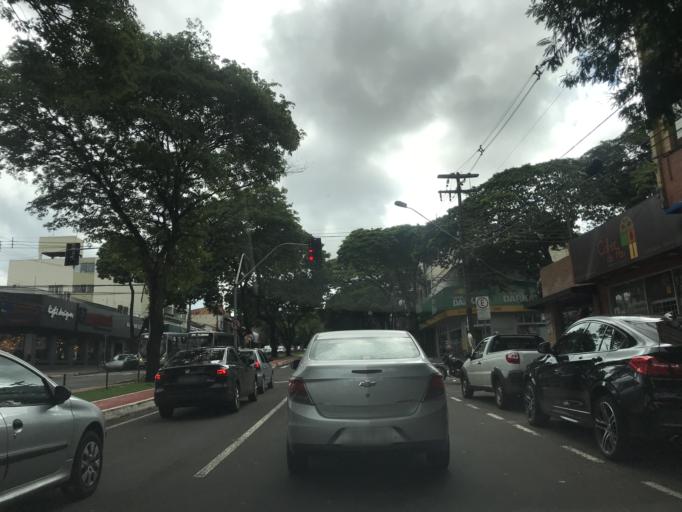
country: BR
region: Parana
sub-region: Maringa
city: Maringa
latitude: -23.4214
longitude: -51.9492
